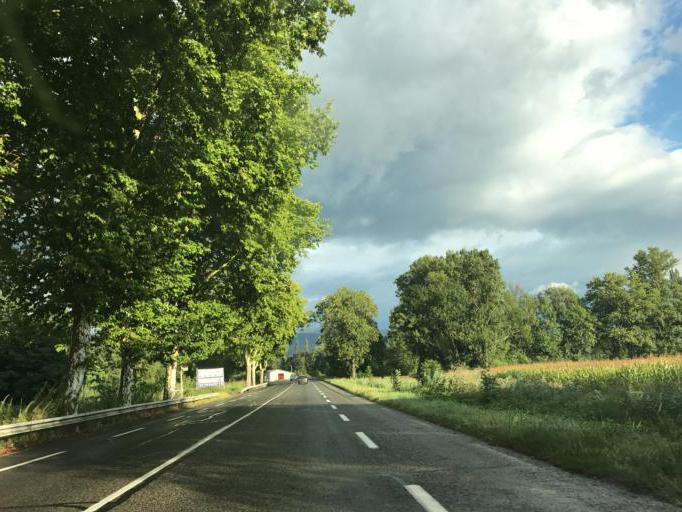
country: FR
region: Rhone-Alpes
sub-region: Departement de la Savoie
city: Les Marches
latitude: 45.5094
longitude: 6.0167
